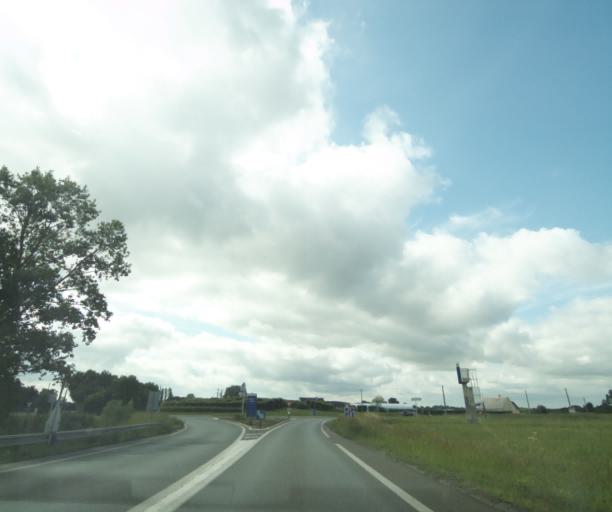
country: FR
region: Pays de la Loire
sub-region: Departement de Maine-et-Loire
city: Vivy
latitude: 47.3092
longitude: -0.0313
